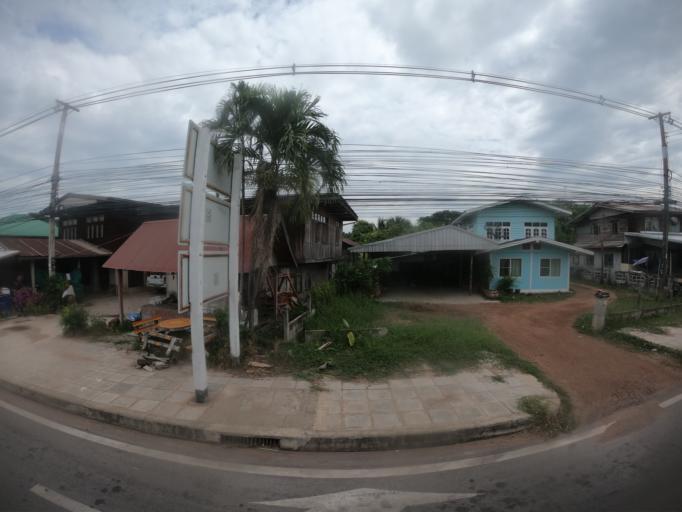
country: TH
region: Maha Sarakham
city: Kantharawichai
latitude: 16.3152
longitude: 103.2998
